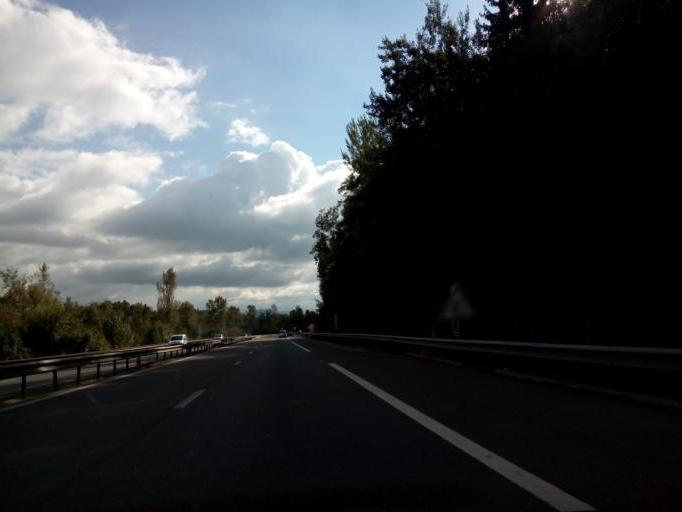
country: FR
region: Rhone-Alpes
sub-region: Departement de la Savoie
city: La Bridoire
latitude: 45.5578
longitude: 5.7582
